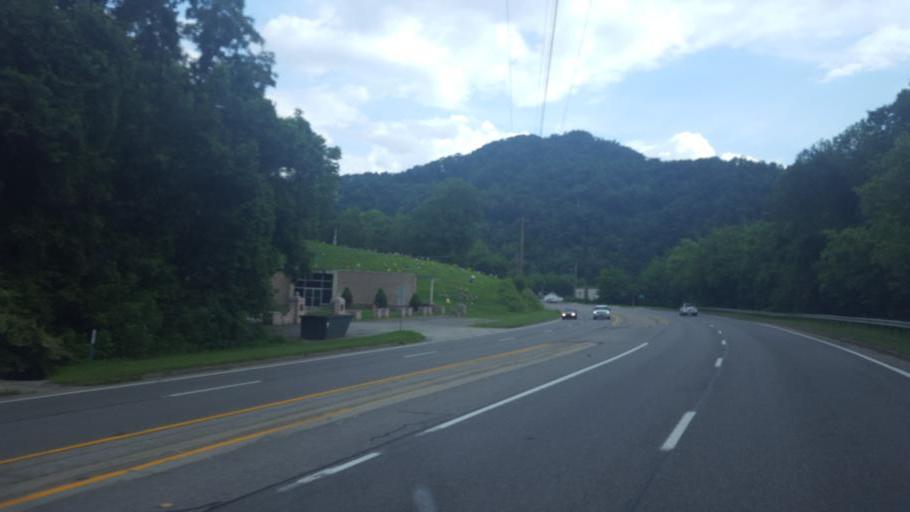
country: US
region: Kentucky
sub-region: Pike County
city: Pikeville
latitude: 37.4473
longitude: -82.5258
